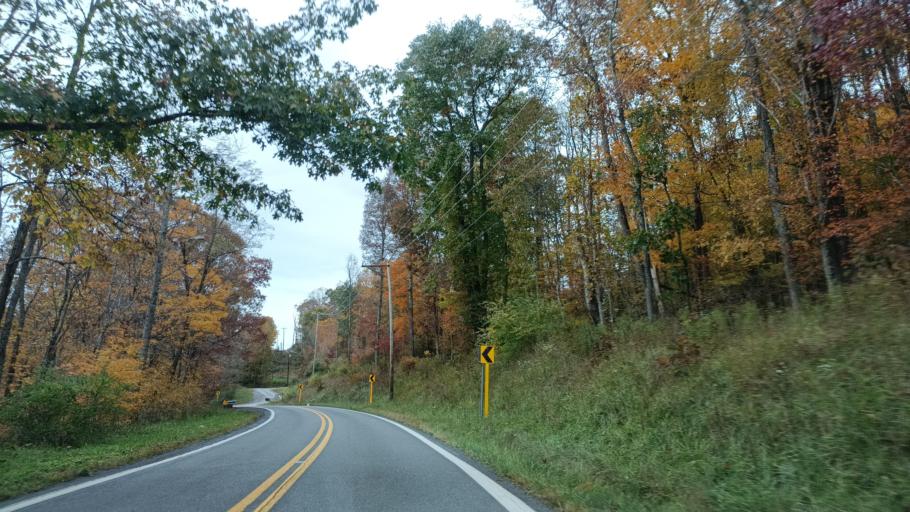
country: US
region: West Virginia
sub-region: Taylor County
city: Grafton
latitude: 39.3339
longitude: -79.8850
